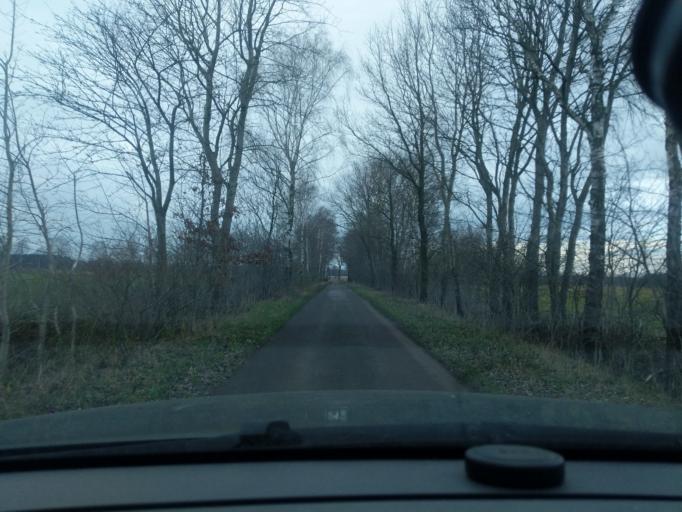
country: DE
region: Lower Saxony
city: Hemslingen
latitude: 53.0971
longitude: 9.6210
